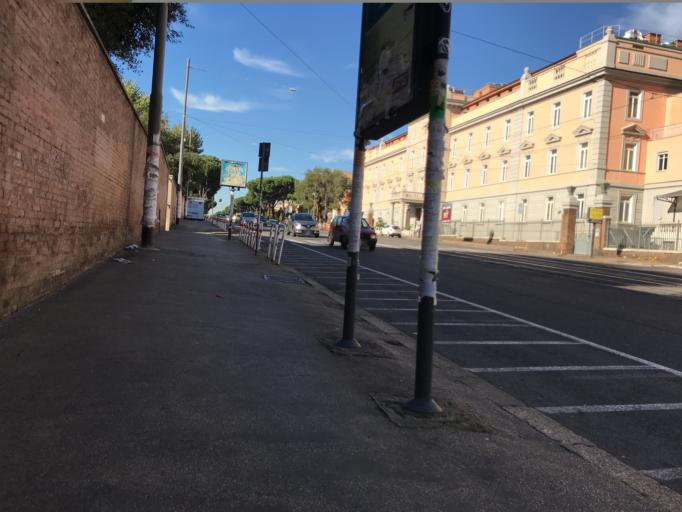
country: IT
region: Latium
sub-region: Citta metropolitana di Roma Capitale
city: Rome
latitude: 41.9046
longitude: 12.5168
